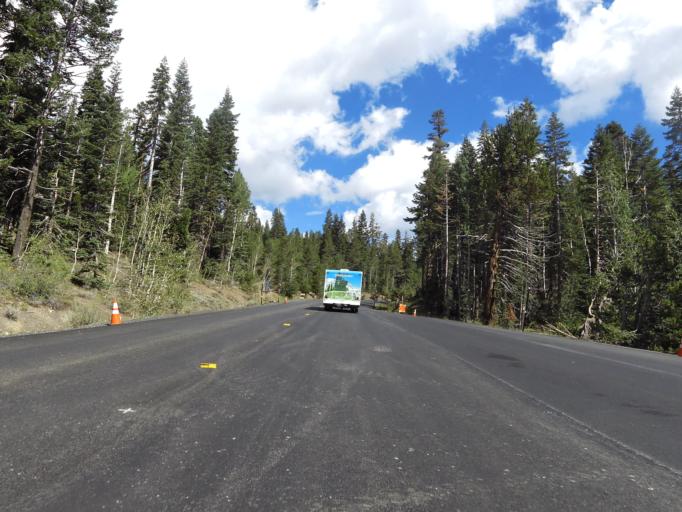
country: US
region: California
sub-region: El Dorado County
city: South Lake Tahoe
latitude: 38.7039
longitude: -120.1124
